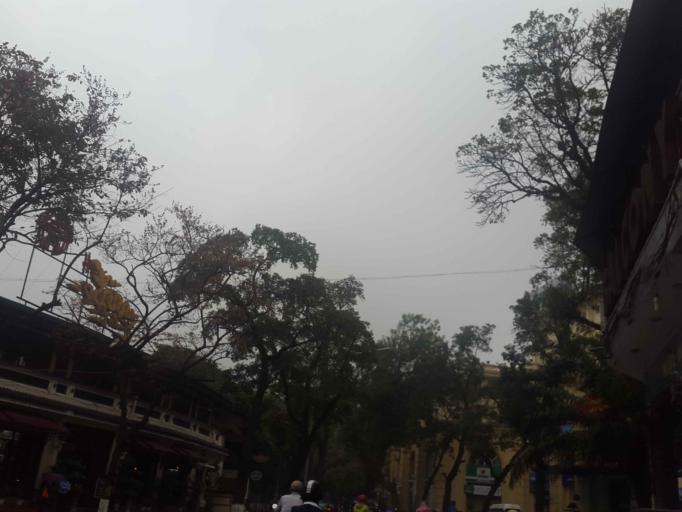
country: VN
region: Ha Noi
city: Hoan Kiem
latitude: 21.0316
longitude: 105.8510
